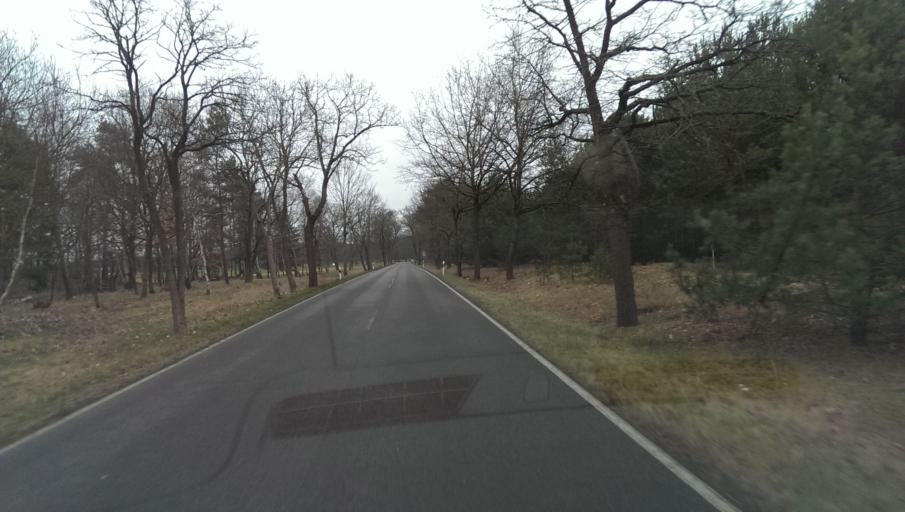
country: DE
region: Brandenburg
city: Mittenwalde
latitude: 52.2181
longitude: 13.5485
